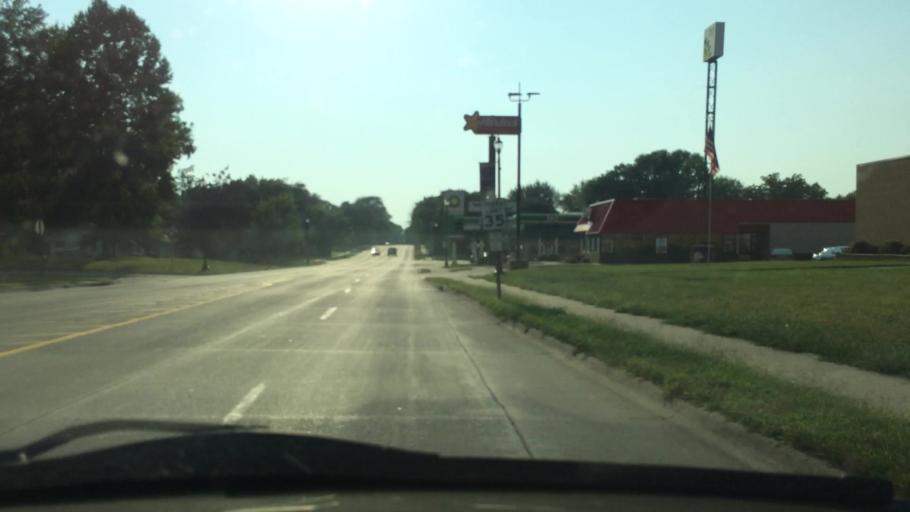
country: US
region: Iowa
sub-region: Henry County
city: Mount Pleasant
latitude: 40.9642
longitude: -91.5400
